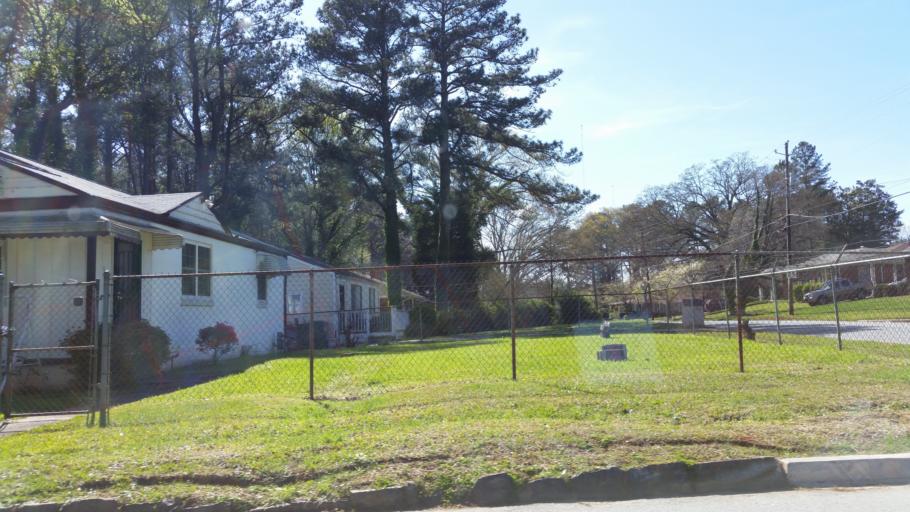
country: US
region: Georgia
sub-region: Fulton County
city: Atlanta
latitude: 33.7601
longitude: -84.4743
